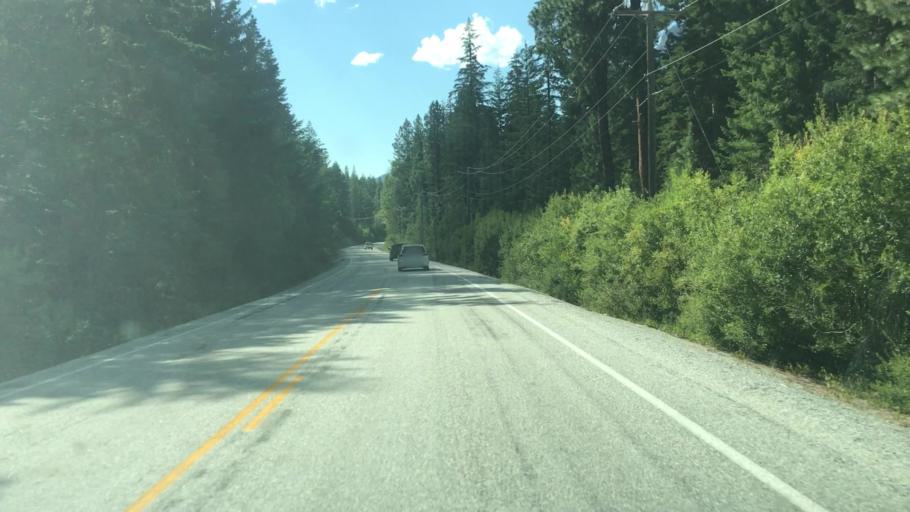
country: US
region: Washington
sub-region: Chelan County
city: Leavenworth
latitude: 47.8242
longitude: -120.7543
